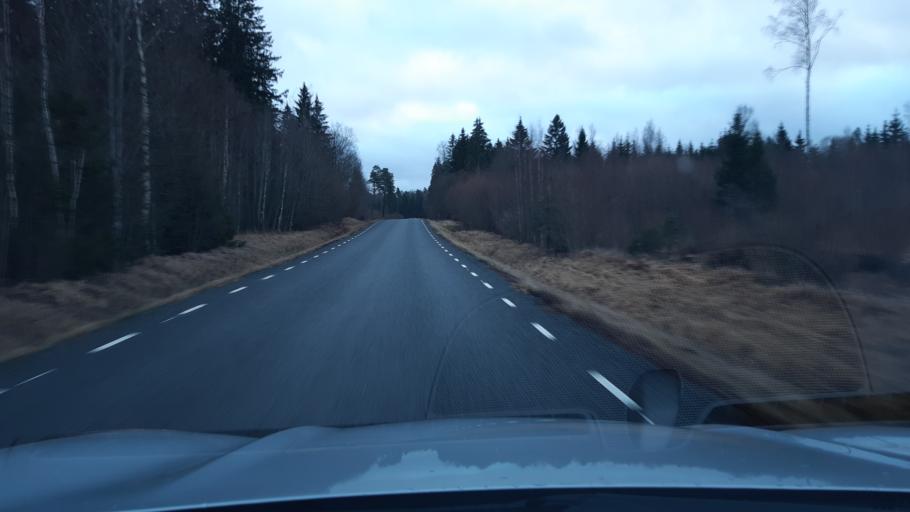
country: EE
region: Harju
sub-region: Saku vald
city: Saku
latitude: 59.1830
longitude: 24.6092
